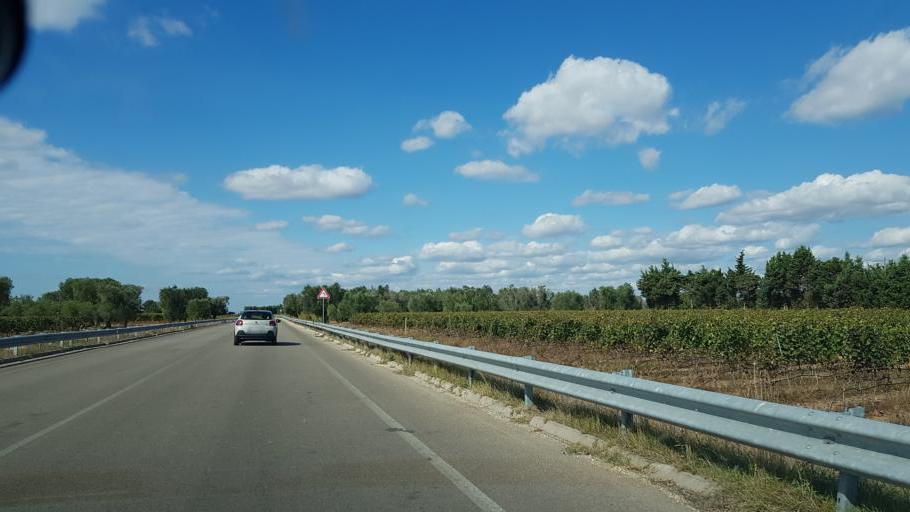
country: IT
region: Apulia
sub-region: Provincia di Lecce
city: Leverano
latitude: 40.3059
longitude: 17.9975
